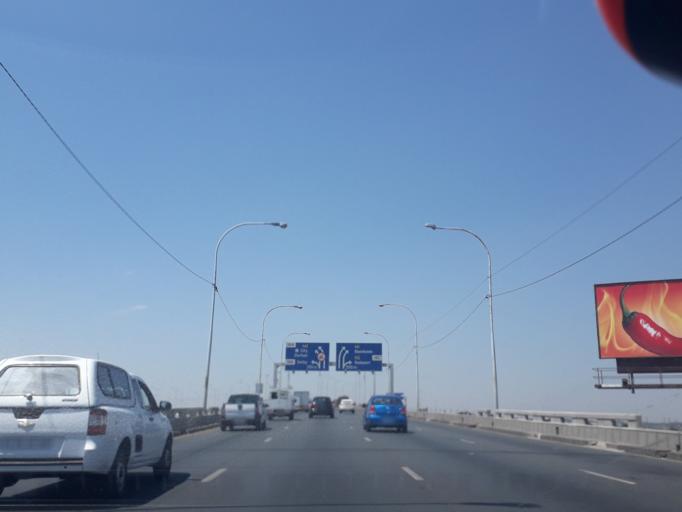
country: ZA
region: Gauteng
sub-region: City of Johannesburg Metropolitan Municipality
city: Johannesburg
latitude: -26.2082
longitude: 28.0307
